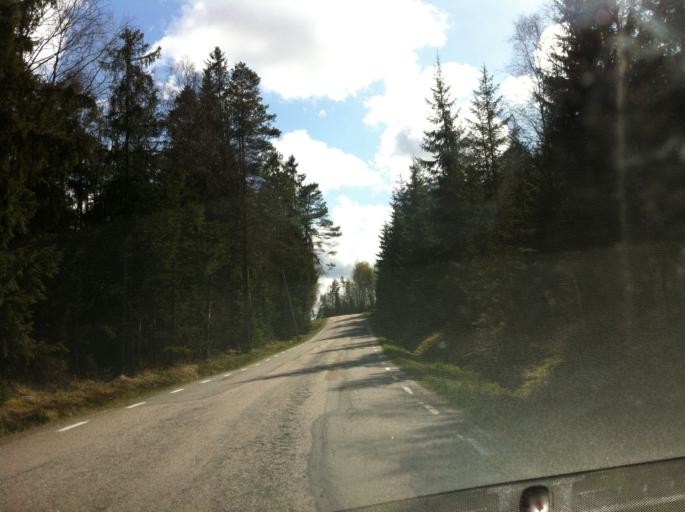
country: SE
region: Vaestra Goetaland
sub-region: Alingsas Kommun
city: Alingsas
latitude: 57.8233
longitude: 12.6460
